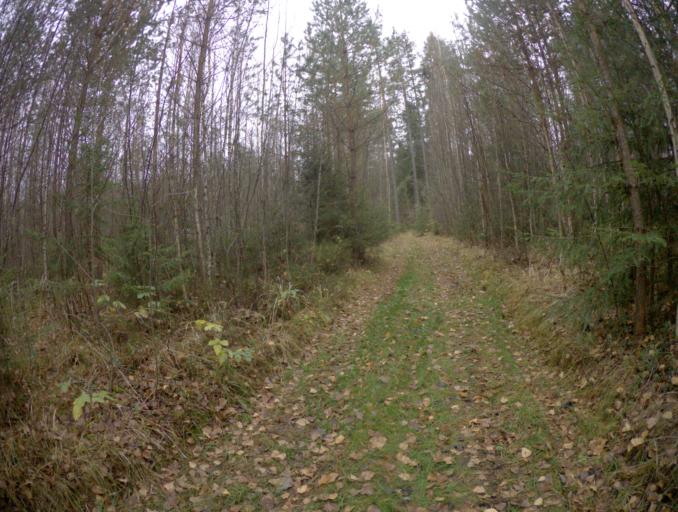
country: RU
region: Vladimir
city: Golovino
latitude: 56.0212
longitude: 40.5234
